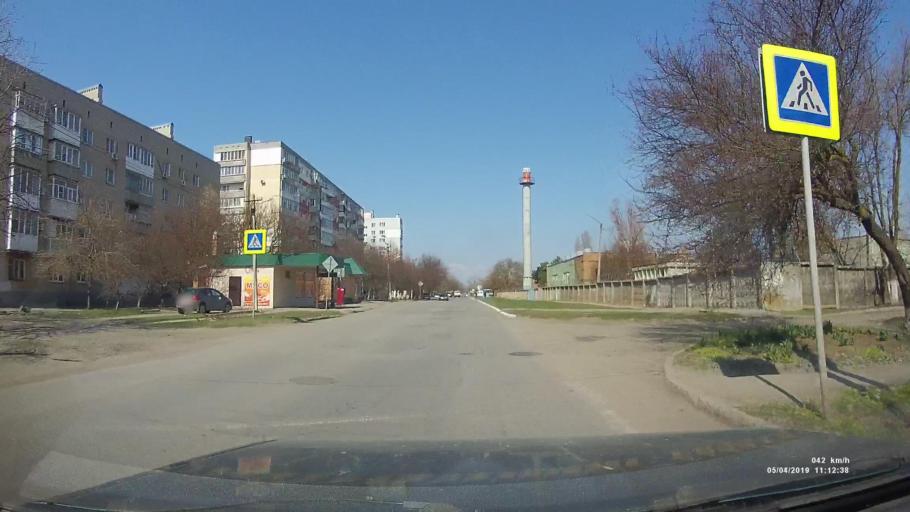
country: RU
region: Rostov
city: Azov
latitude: 47.0988
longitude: 39.4362
